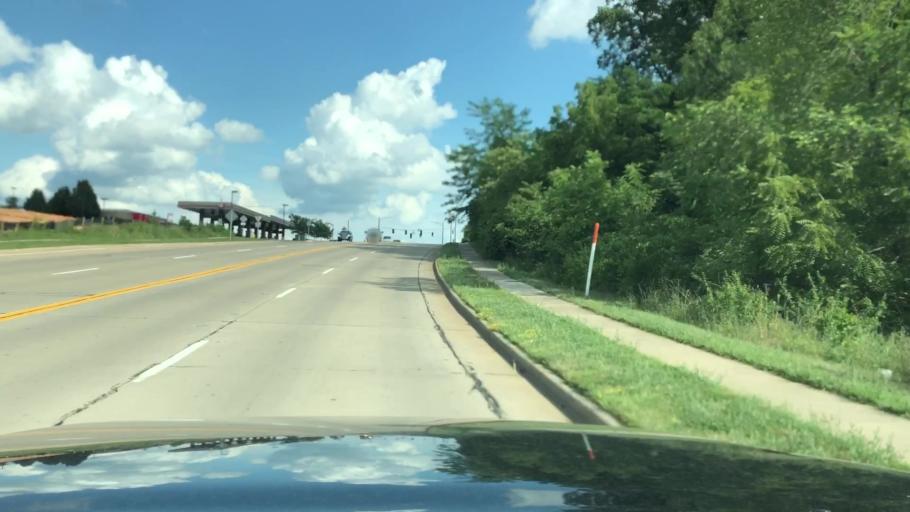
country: US
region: Missouri
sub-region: Saint Charles County
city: Wentzville
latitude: 38.8238
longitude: -90.8550
